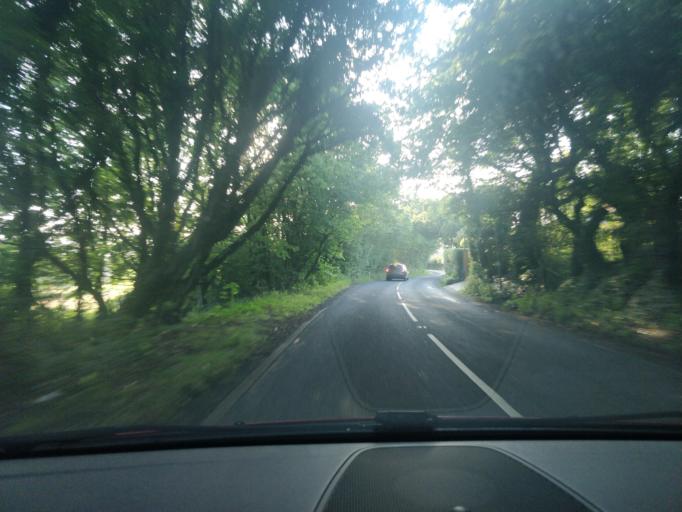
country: GB
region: England
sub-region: Lancashire
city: Skelmersdale
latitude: 53.5646
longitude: -2.7568
